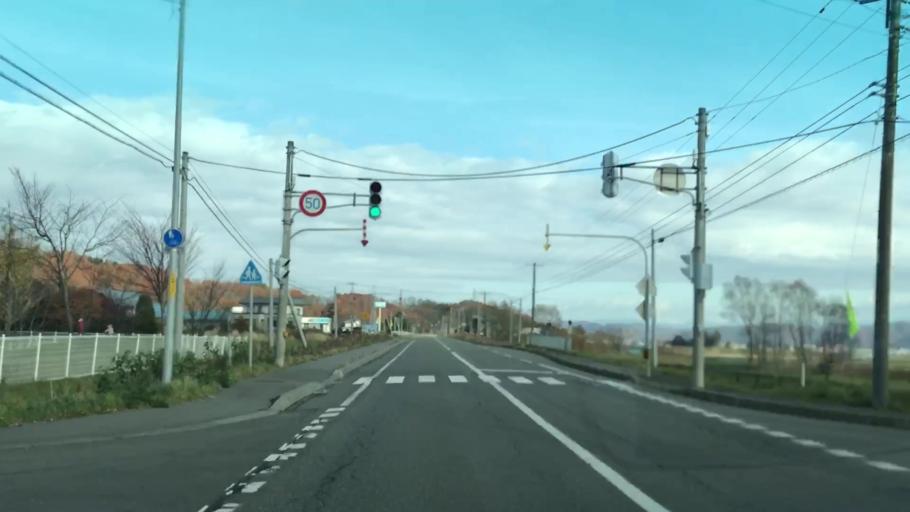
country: JP
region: Hokkaido
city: Shizunai-furukawacho
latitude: 42.5556
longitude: 142.0771
